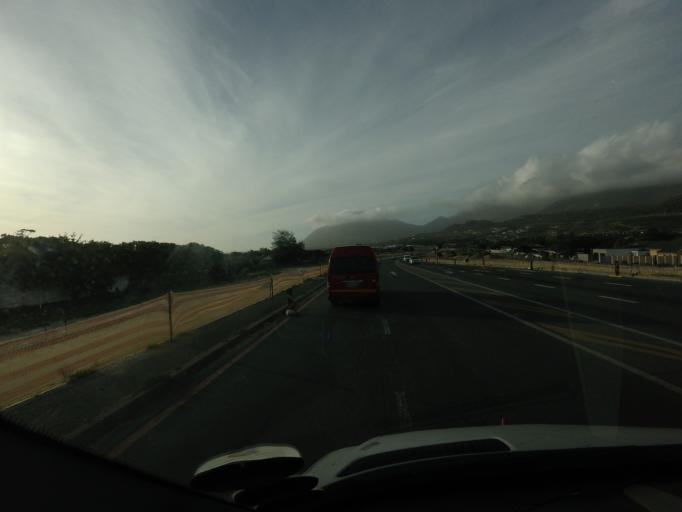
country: ZA
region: Western Cape
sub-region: City of Cape Town
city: Bergvliet
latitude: -34.1289
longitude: 18.3934
